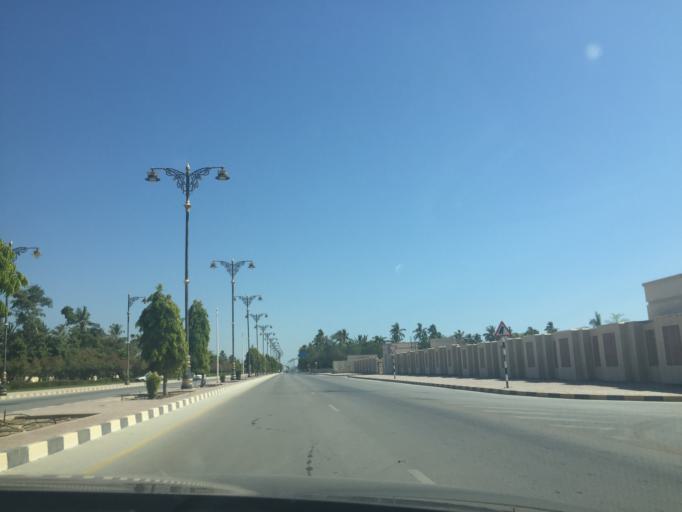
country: OM
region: Zufar
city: Salalah
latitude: 17.0261
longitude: 54.1509
